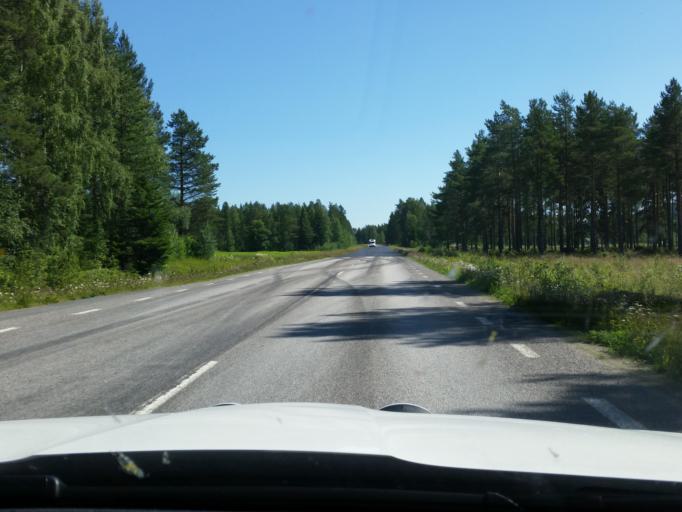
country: SE
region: Norrbotten
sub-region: Alvsbyns Kommun
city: AElvsbyn
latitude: 65.6773
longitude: 20.8261
